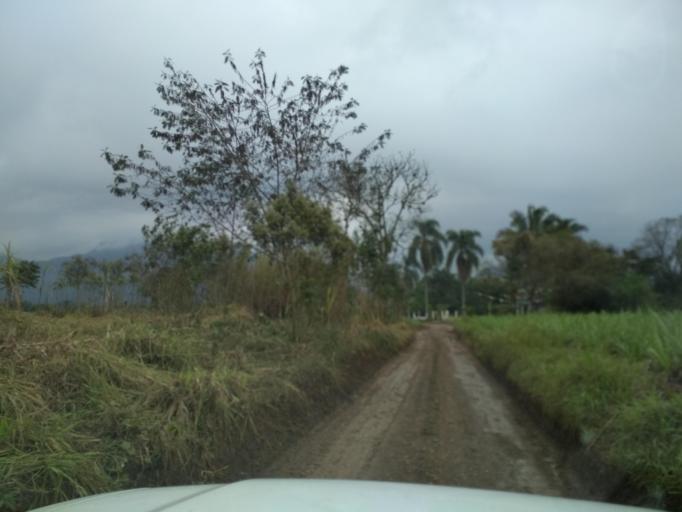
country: MX
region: Veracruz
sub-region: Cordoba
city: San Jose de Tapia
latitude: 18.8506
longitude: -96.9697
